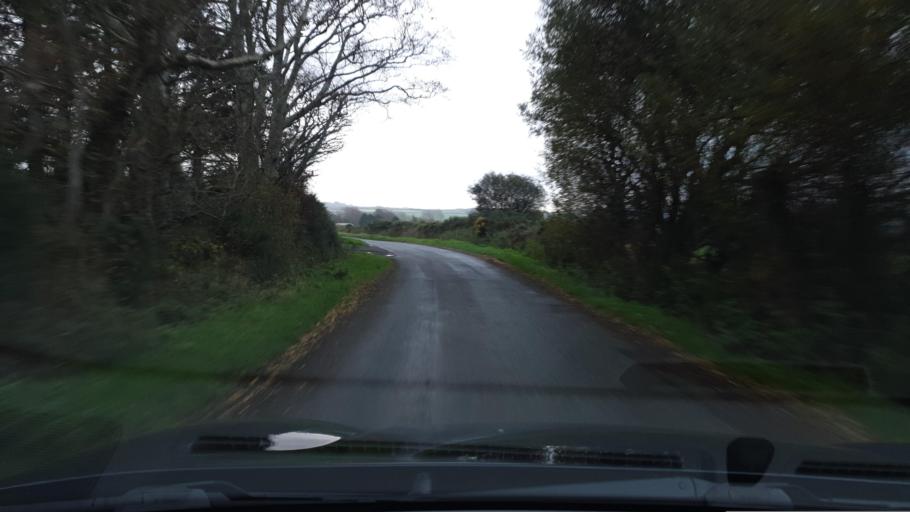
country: IE
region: Leinster
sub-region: Wicklow
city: Enniskerry
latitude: 53.1202
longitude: -6.1944
